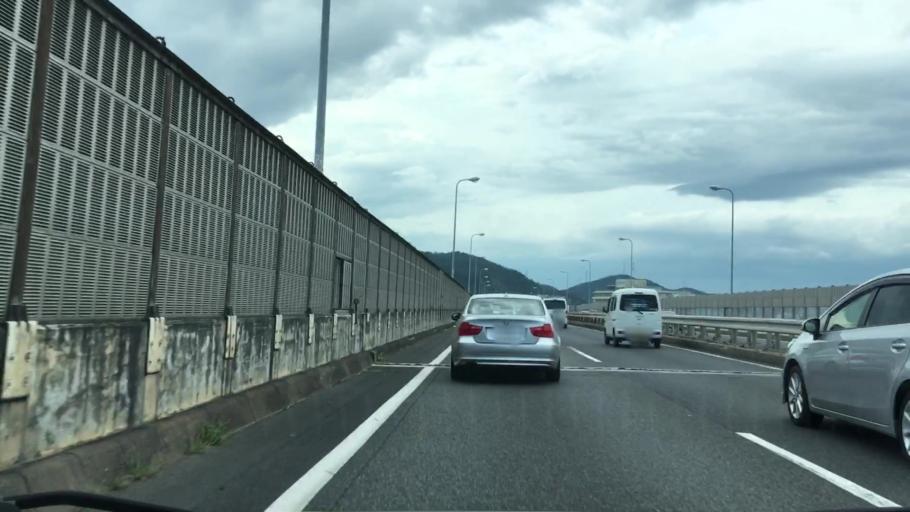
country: JP
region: Hyogo
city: Kakogawacho-honmachi
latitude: 34.7867
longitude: 134.7769
